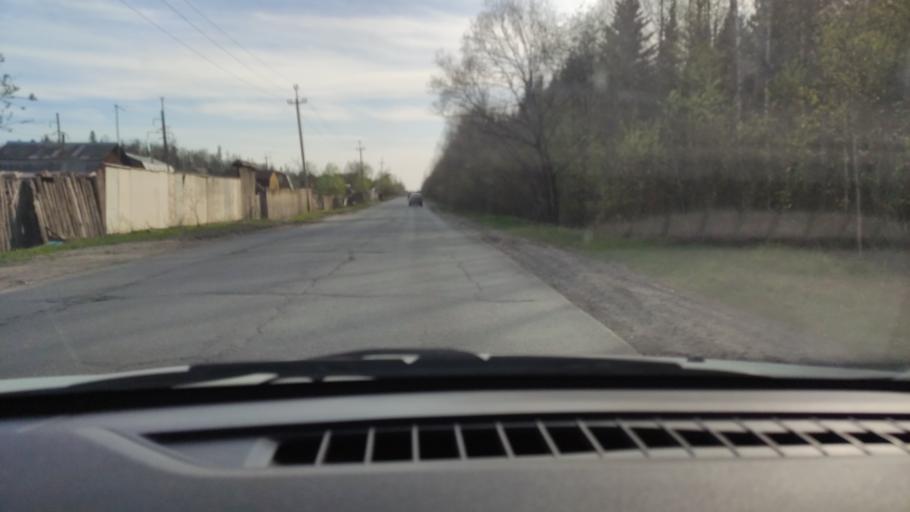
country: RU
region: Perm
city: Novyye Lyady
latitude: 57.9400
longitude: 56.4922
